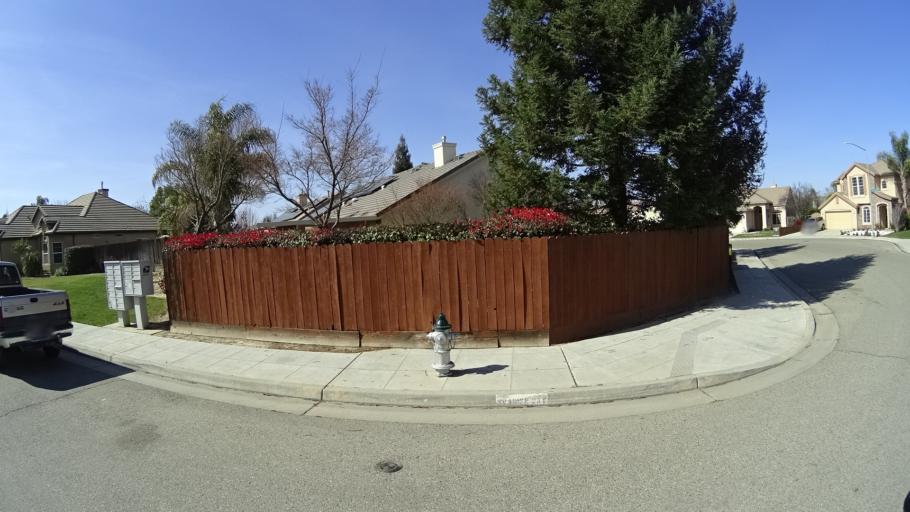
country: US
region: California
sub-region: Fresno County
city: Clovis
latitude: 36.8916
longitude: -119.7616
